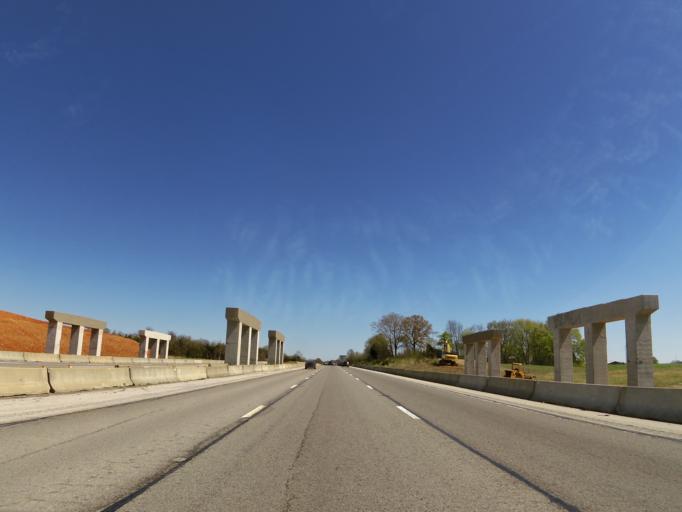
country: US
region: Kentucky
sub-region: Warren County
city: Bowling Green
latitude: 37.0116
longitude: -86.3276
